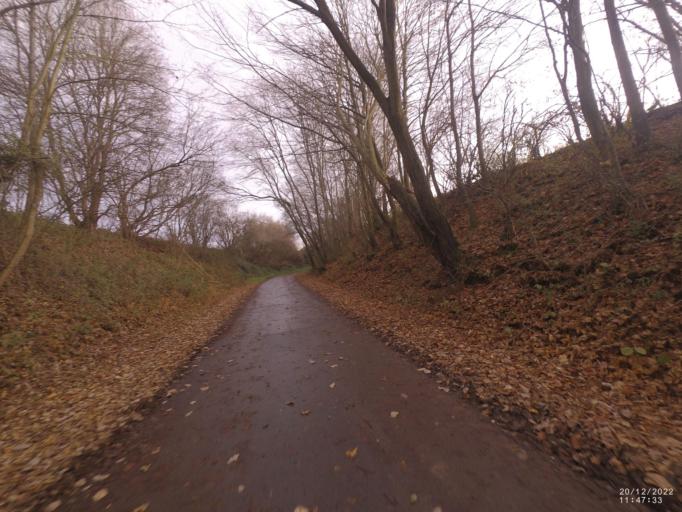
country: DE
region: Rheinland-Pfalz
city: Konigsfeld
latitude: 50.5338
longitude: 7.1965
